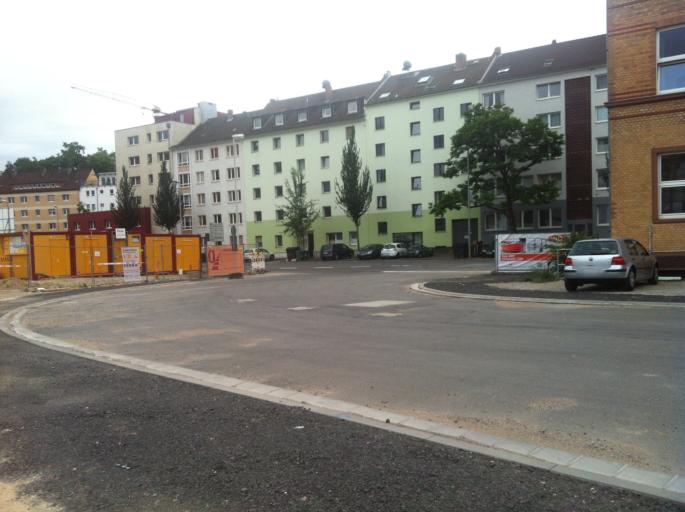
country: DE
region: Rheinland-Pfalz
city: Mainz
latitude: 50.0048
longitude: 8.2538
